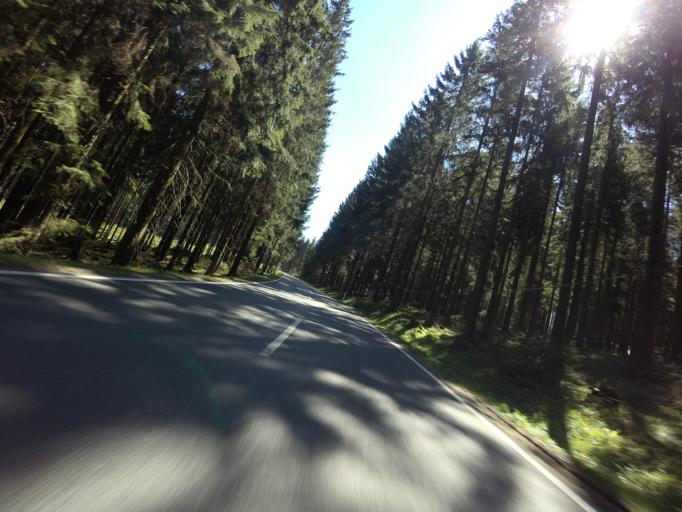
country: DE
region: North Rhine-Westphalia
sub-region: Regierungsbezirk Arnsberg
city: Kirchhundem
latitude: 51.0699
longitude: 8.1849
